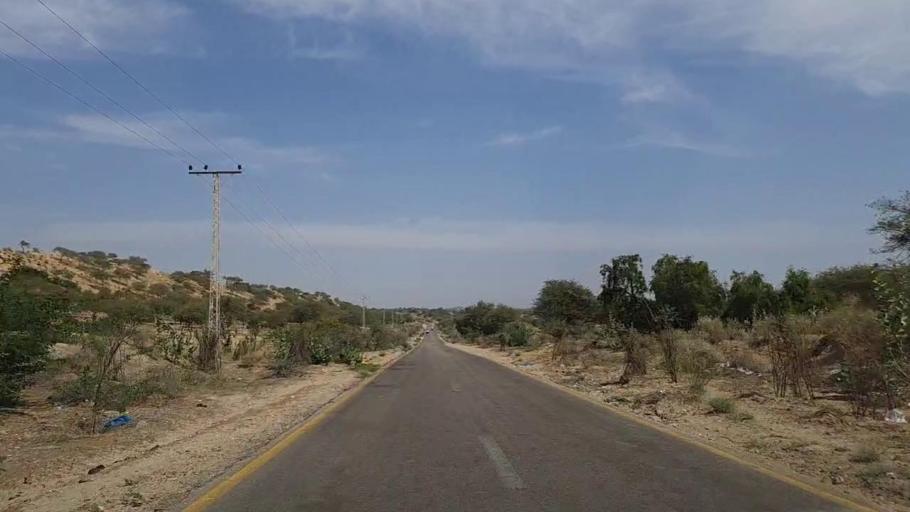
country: PK
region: Sindh
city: Mithi
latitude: 24.7748
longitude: 69.8041
